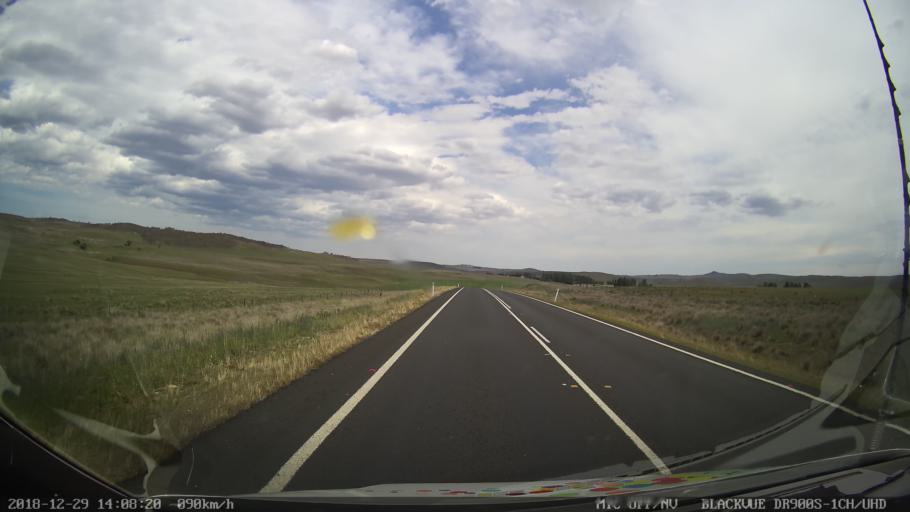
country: AU
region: New South Wales
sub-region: Cooma-Monaro
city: Cooma
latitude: -36.3639
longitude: 149.2143
